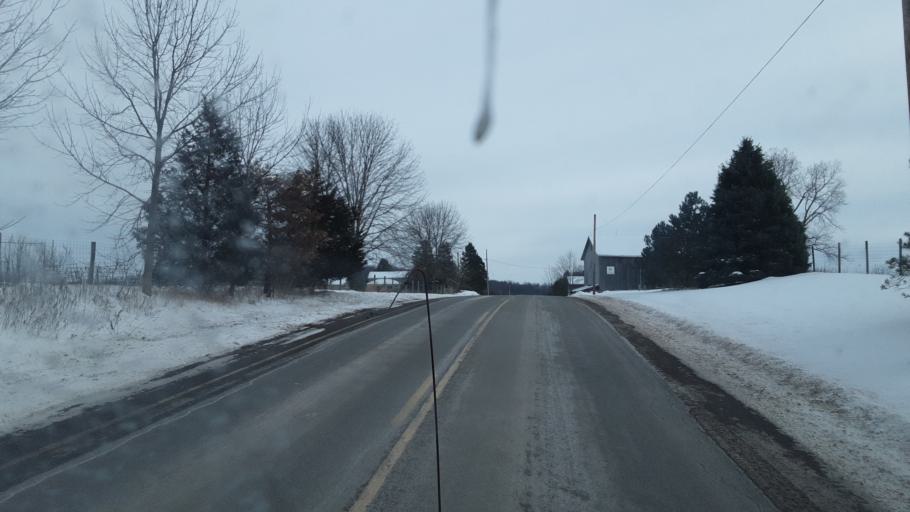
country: US
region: New York
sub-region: Wayne County
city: Newark
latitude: 43.0906
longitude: -77.0500
